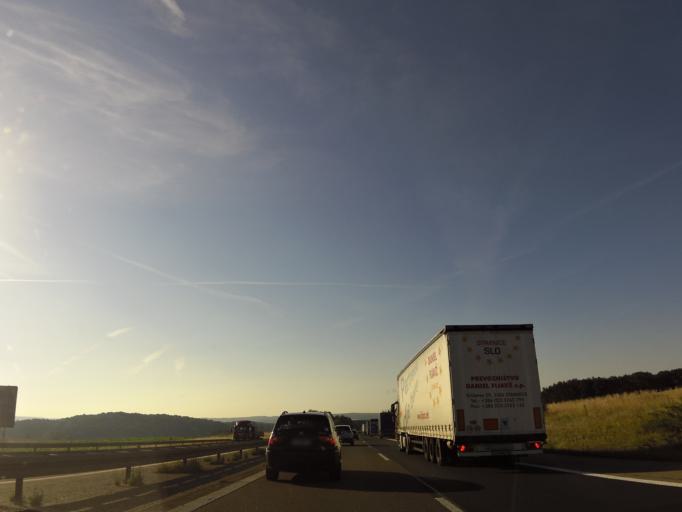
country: DE
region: Bavaria
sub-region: Regierungsbezirk Mittelfranken
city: Gremsdorf
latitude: 49.7186
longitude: 10.8346
